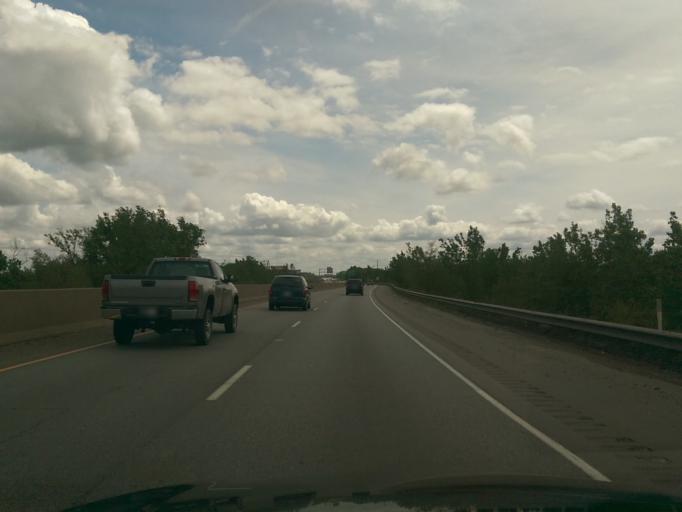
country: US
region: Indiana
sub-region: Lake County
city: East Chicago
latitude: 41.5990
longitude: -87.4327
